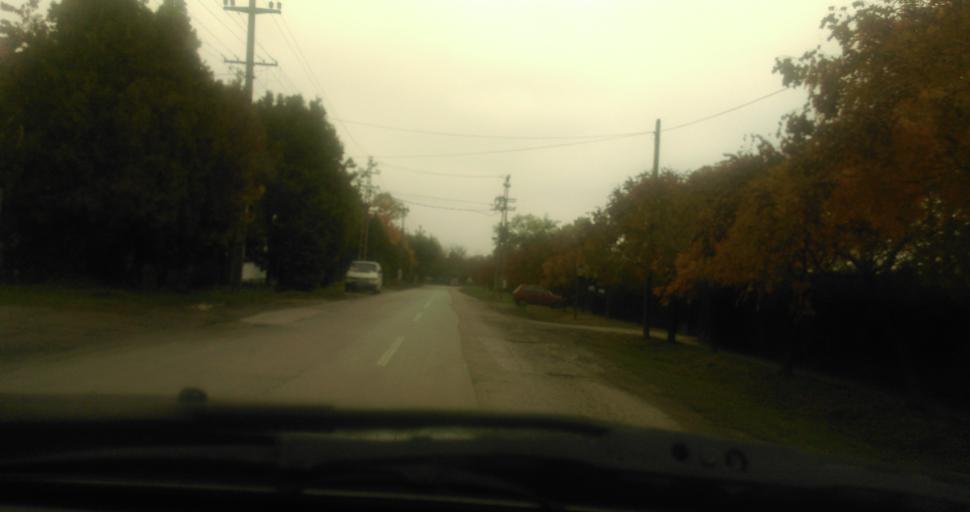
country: RS
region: Autonomna Pokrajina Vojvodina
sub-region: Juznobacki Okrug
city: Becej
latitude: 45.6155
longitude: 20.0333
